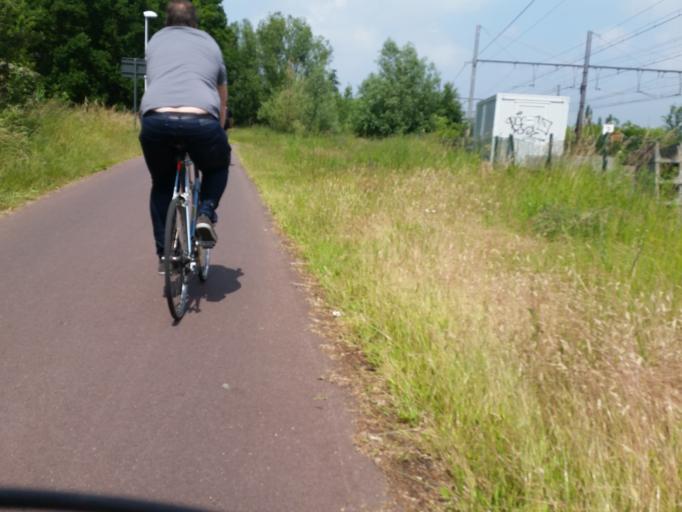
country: BE
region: Flanders
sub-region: Provincie Antwerpen
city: Hove
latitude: 51.1373
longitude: 4.4745
